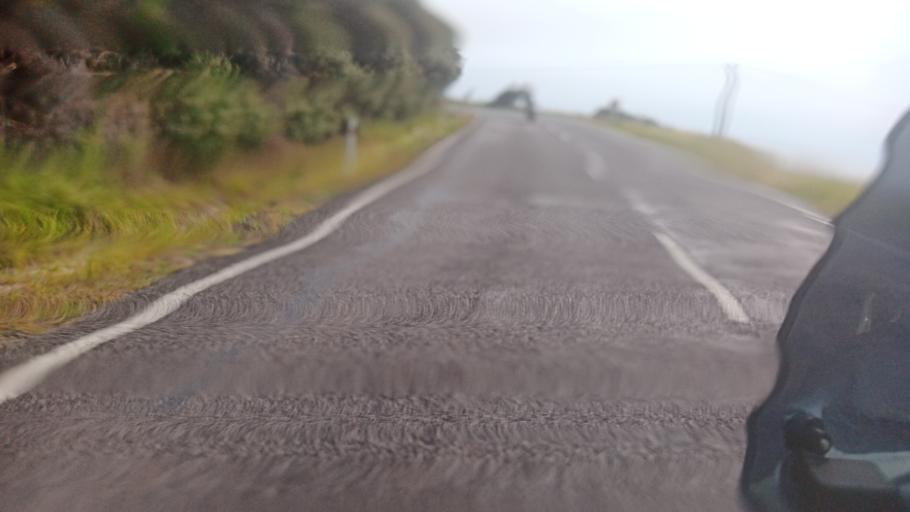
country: NZ
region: Bay of Plenty
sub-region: Opotiki District
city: Opotiki
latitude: -37.6671
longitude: 177.8058
